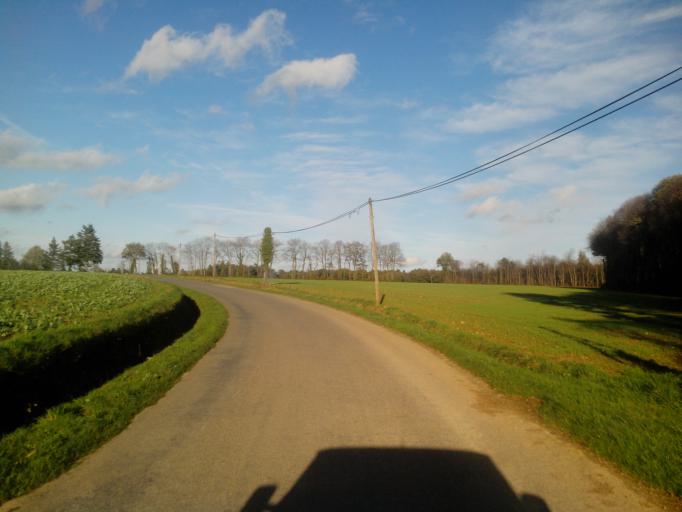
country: FR
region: Brittany
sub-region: Departement du Morbihan
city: Guilliers
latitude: 48.0879
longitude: -2.4115
